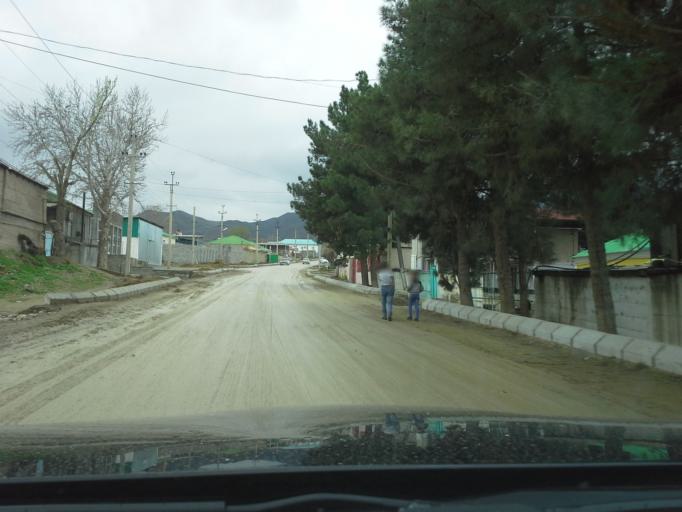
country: TM
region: Ahal
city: Abadan
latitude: 37.9587
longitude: 58.2090
